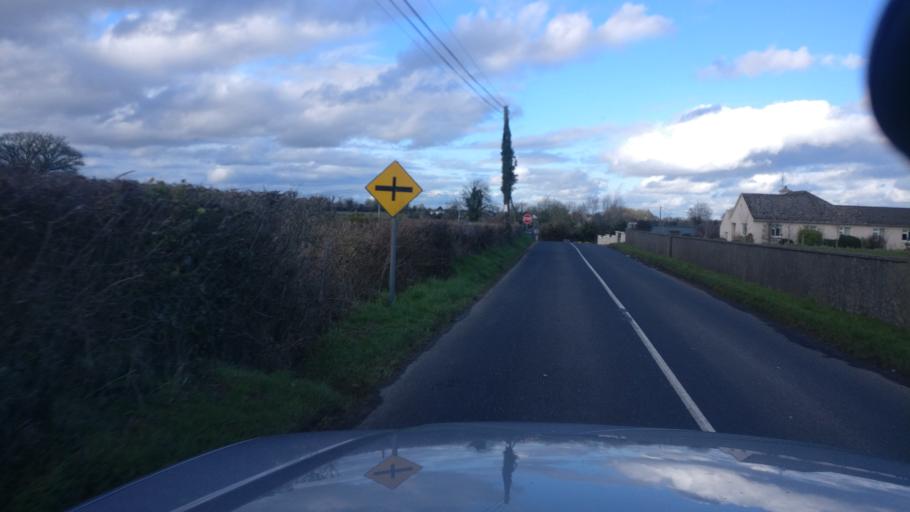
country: IE
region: Connaught
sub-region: County Galway
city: Loughrea
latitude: 53.2227
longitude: -8.3942
